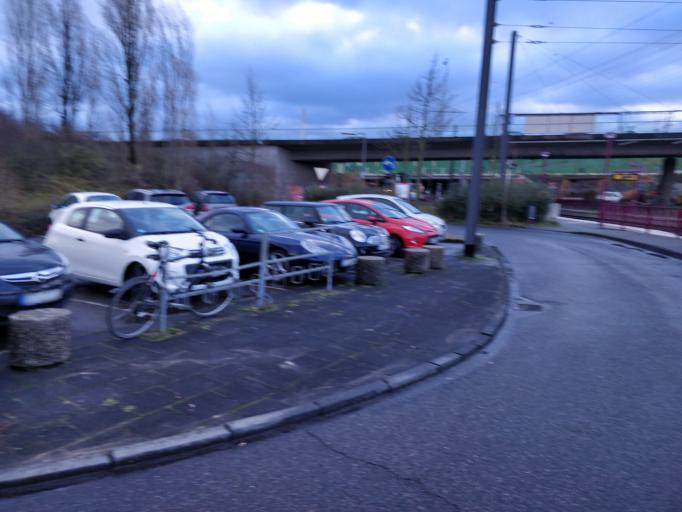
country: DE
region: North Rhine-Westphalia
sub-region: Regierungsbezirk Koln
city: Leverkusen
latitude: 51.0285
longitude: 6.9479
